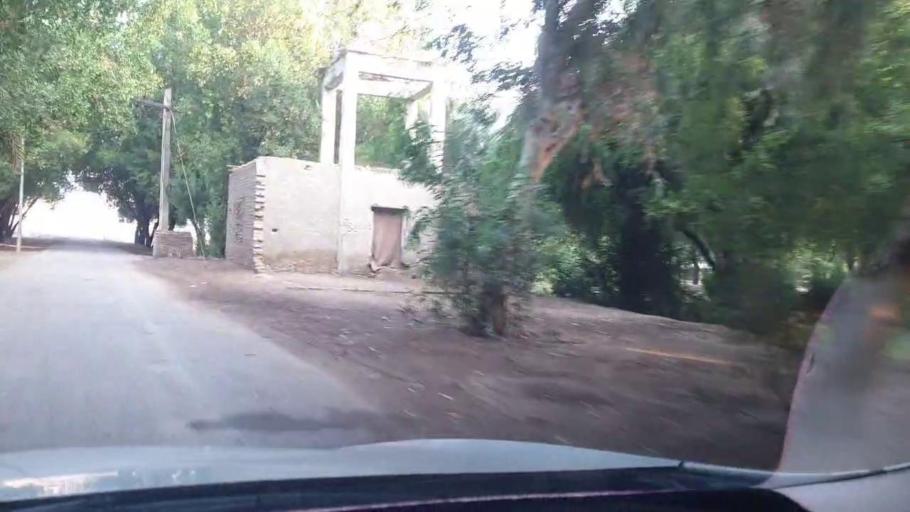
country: PK
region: Sindh
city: Sehwan
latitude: 26.3974
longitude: 67.8612
